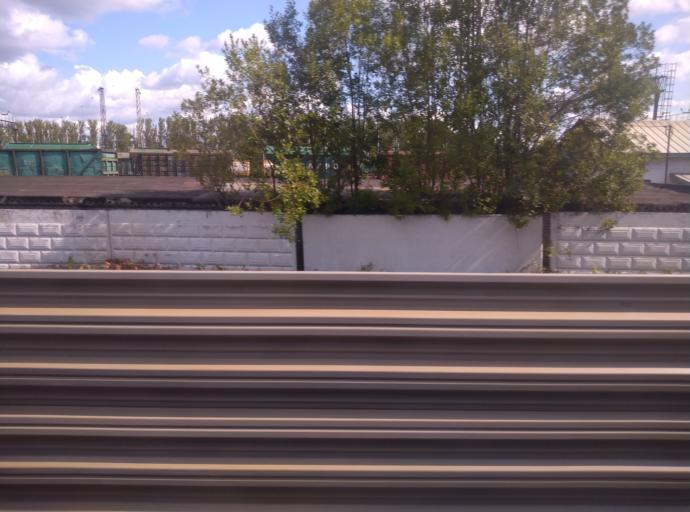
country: RU
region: St.-Petersburg
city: Kupchino
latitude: 59.8818
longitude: 30.4045
